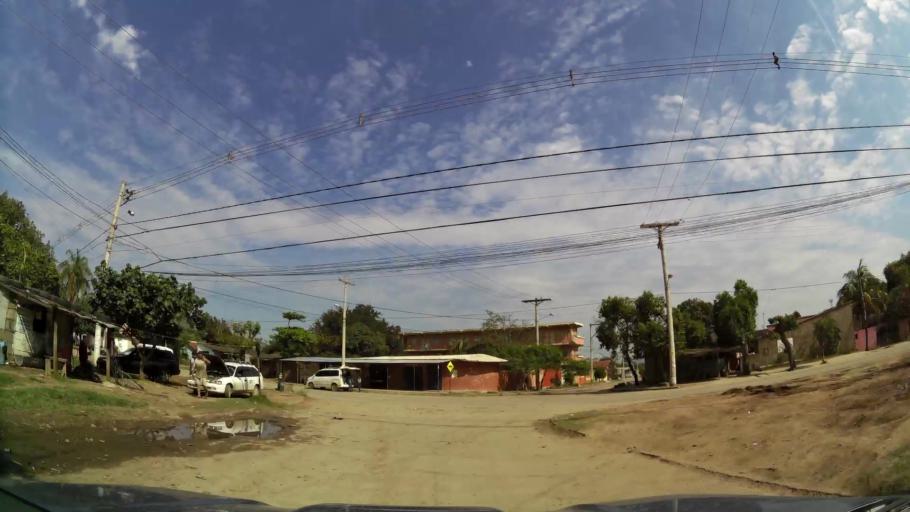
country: BO
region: Santa Cruz
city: Santa Cruz de la Sierra
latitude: -17.7250
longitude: -63.1553
